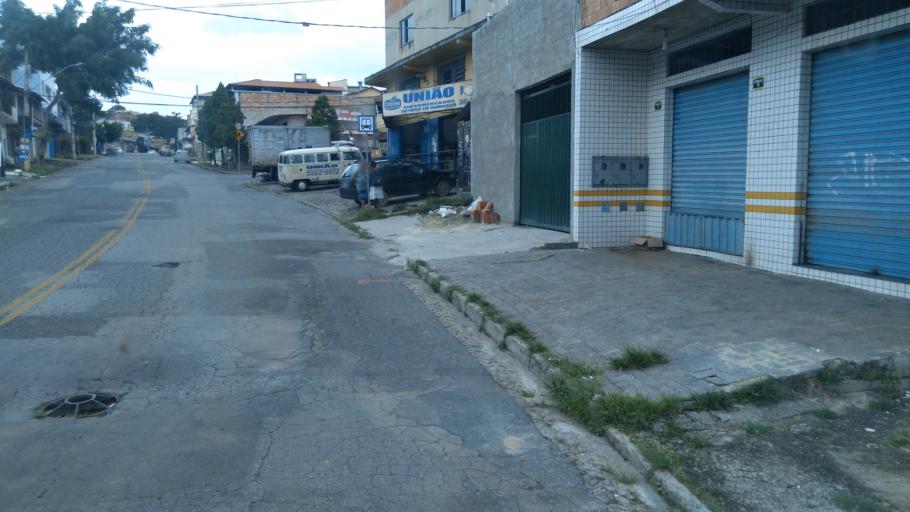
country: BR
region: Minas Gerais
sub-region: Belo Horizonte
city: Belo Horizonte
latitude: -19.8482
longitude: -43.9077
